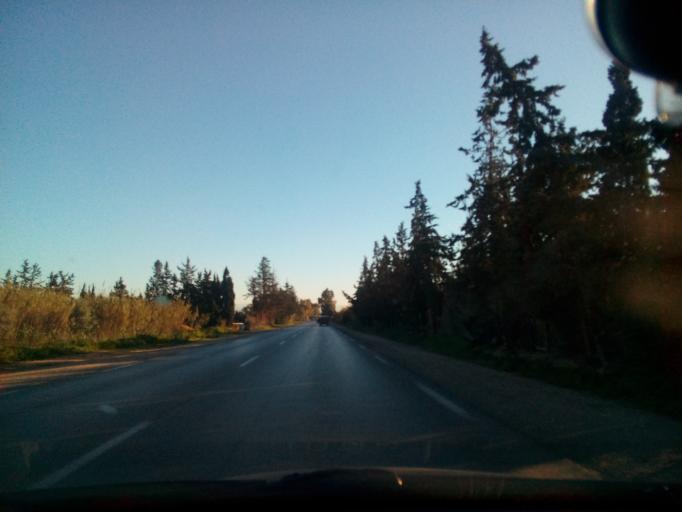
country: DZ
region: Mostaganem
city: Mostaganem
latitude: 35.8051
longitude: 0.1716
